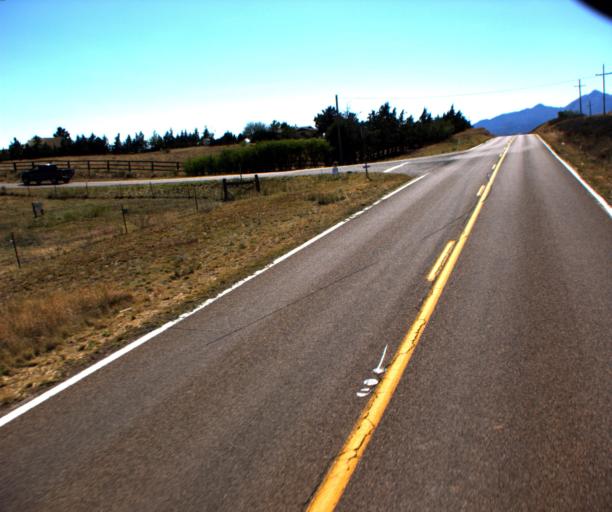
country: US
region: Arizona
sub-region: Cochise County
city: Huachuca City
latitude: 31.6736
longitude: -110.6276
